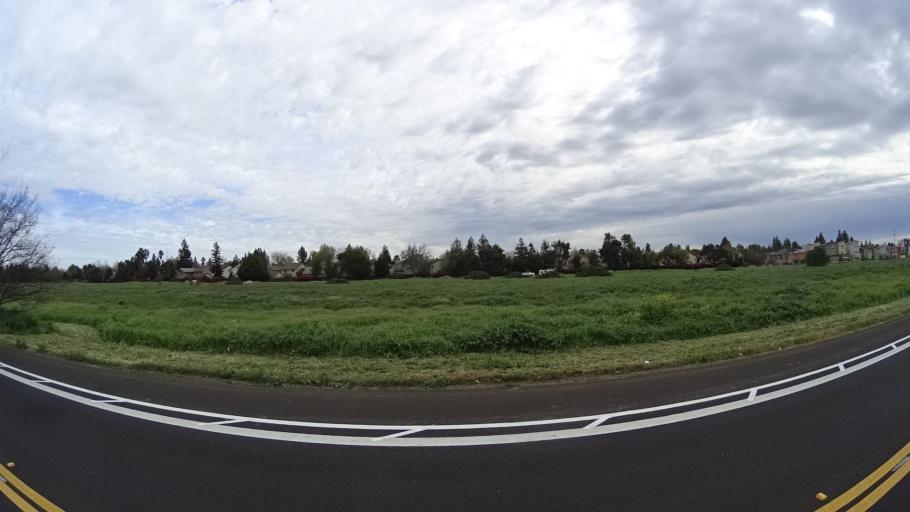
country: US
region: California
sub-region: Yolo County
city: Davis
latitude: 38.5487
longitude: -121.7101
